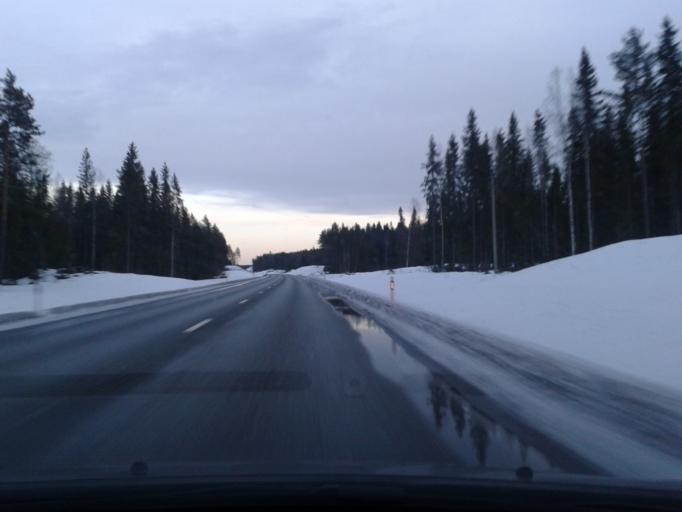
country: SE
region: Vaesternorrland
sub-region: Kramfors Kommun
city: Bollstabruk
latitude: 63.0711
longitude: 17.5680
